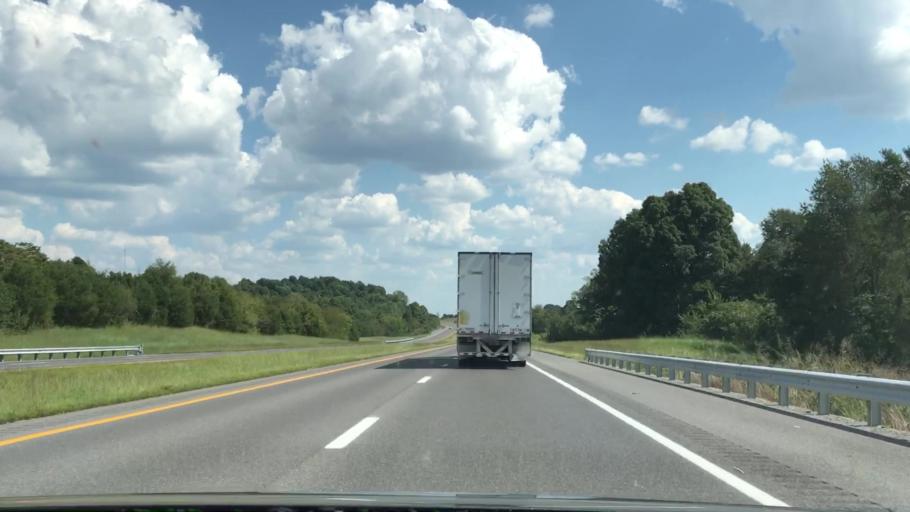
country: US
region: Kentucky
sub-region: Caldwell County
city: Princeton
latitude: 37.1104
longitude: -87.9592
